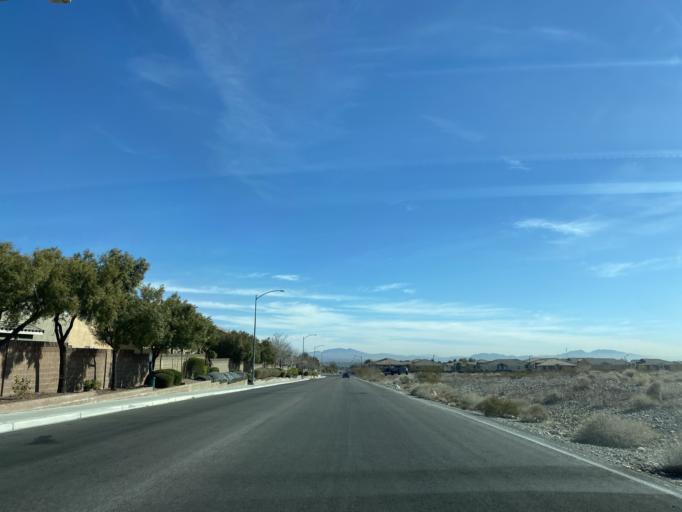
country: US
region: Nevada
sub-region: Clark County
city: Summerlin South
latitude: 36.3030
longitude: -115.3040
